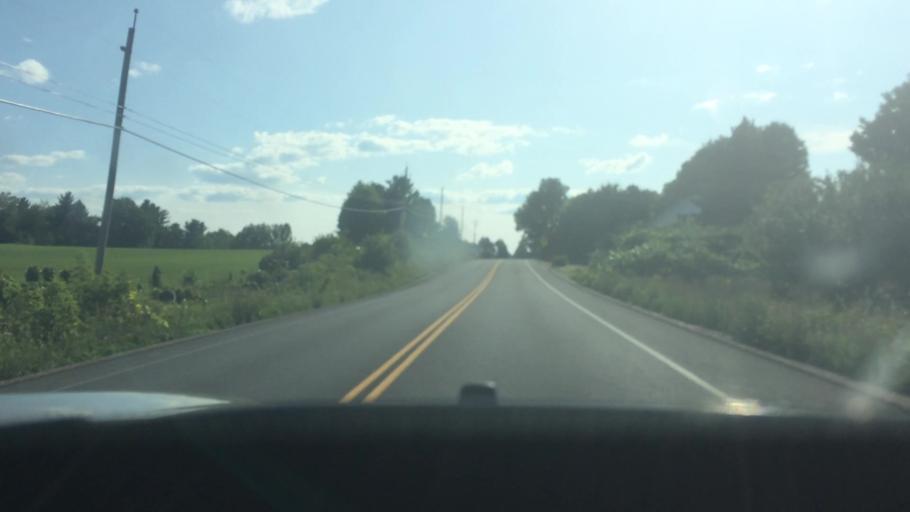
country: US
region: New York
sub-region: Franklin County
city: Malone
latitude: 44.7815
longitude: -74.4936
